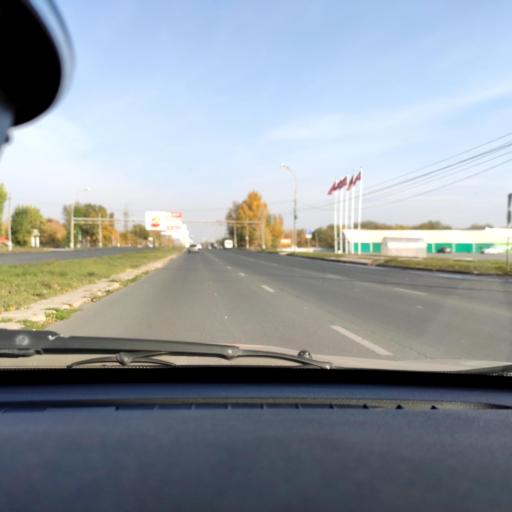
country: RU
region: Samara
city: Tol'yatti
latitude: 53.5430
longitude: 49.2852
